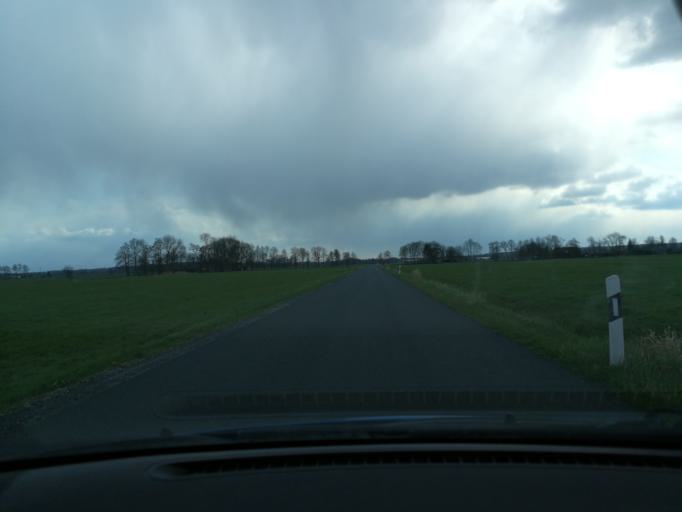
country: DE
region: Lower Saxony
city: Stelle
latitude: 53.4426
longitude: 10.0619
